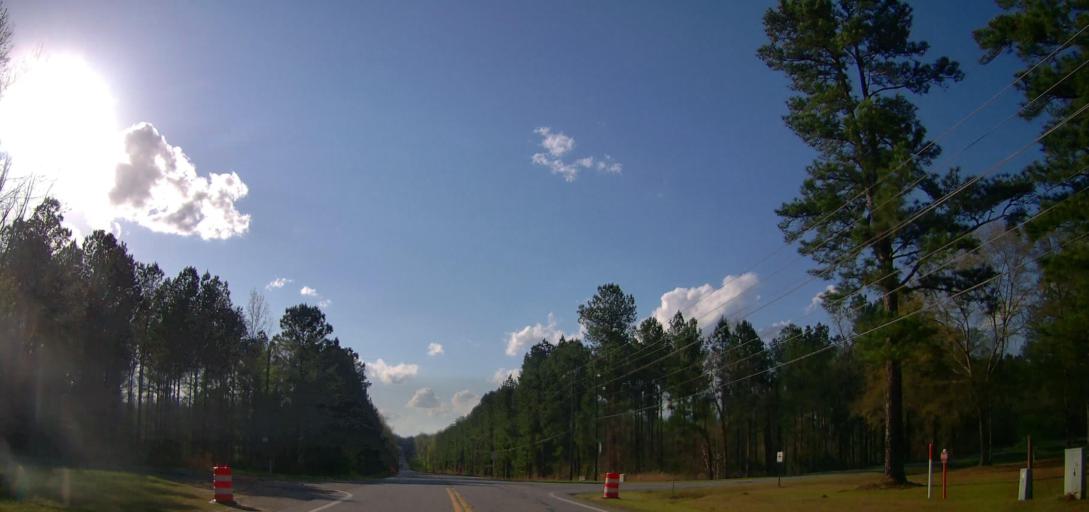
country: US
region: Georgia
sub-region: Putnam County
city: Eatonton
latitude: 33.1712
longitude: -83.3909
